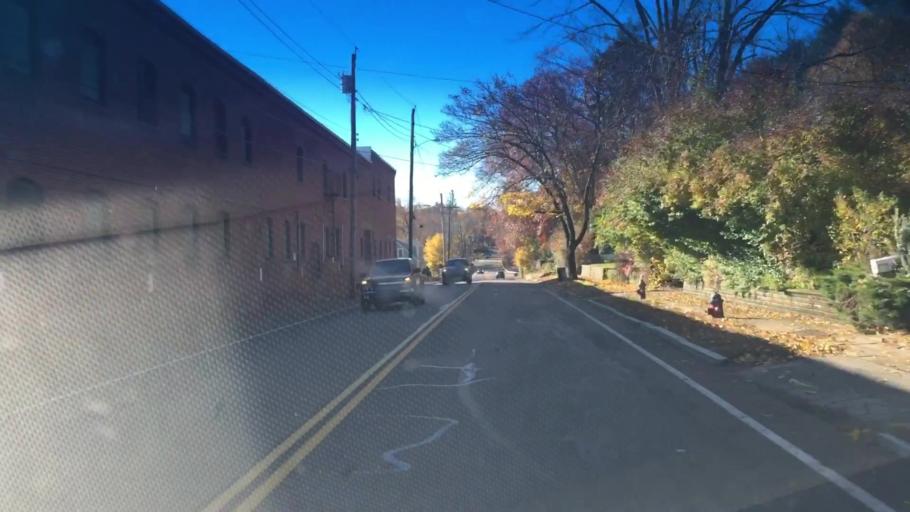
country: US
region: Massachusetts
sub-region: Norfolk County
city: Norwood
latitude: 42.1650
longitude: -71.2137
